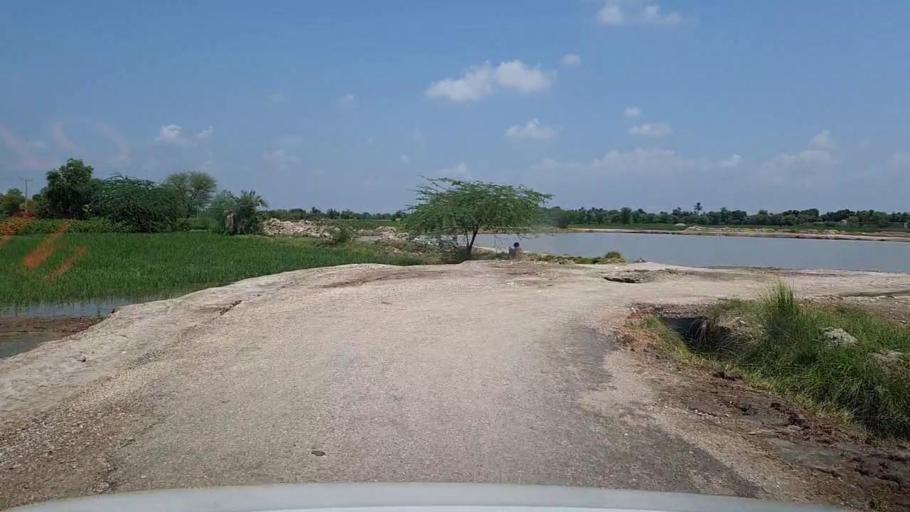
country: PK
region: Sindh
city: Kandiaro
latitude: 26.9863
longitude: 68.2344
